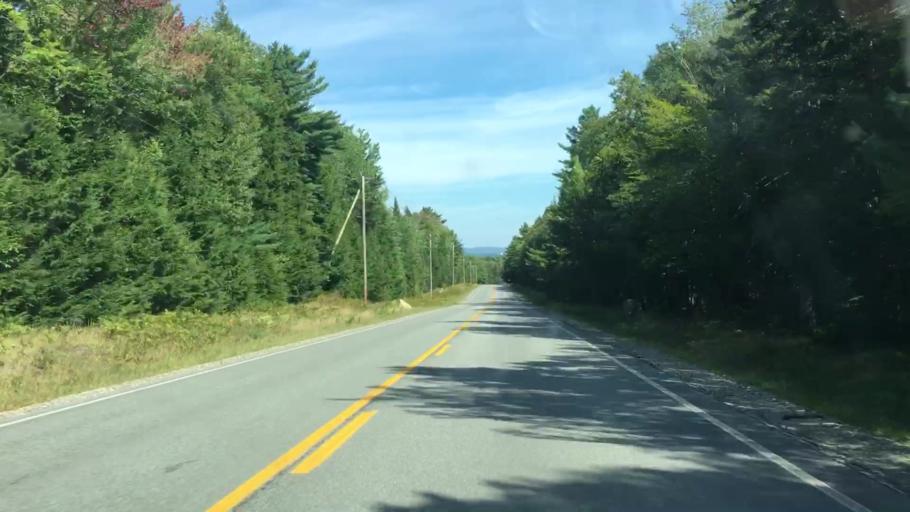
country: US
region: Maine
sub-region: Penobscot County
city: Howland
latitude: 45.2338
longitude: -68.7501
